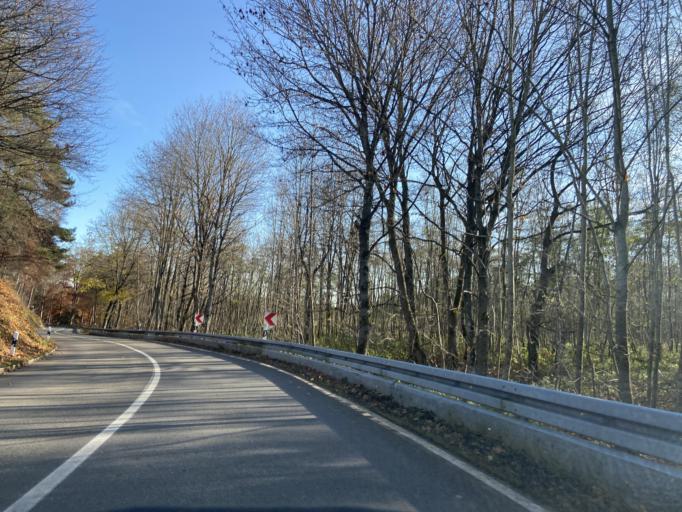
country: DE
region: Baden-Wuerttemberg
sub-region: Tuebingen Region
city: Stetten am Kalten Markt
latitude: 48.1114
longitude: 9.0822
